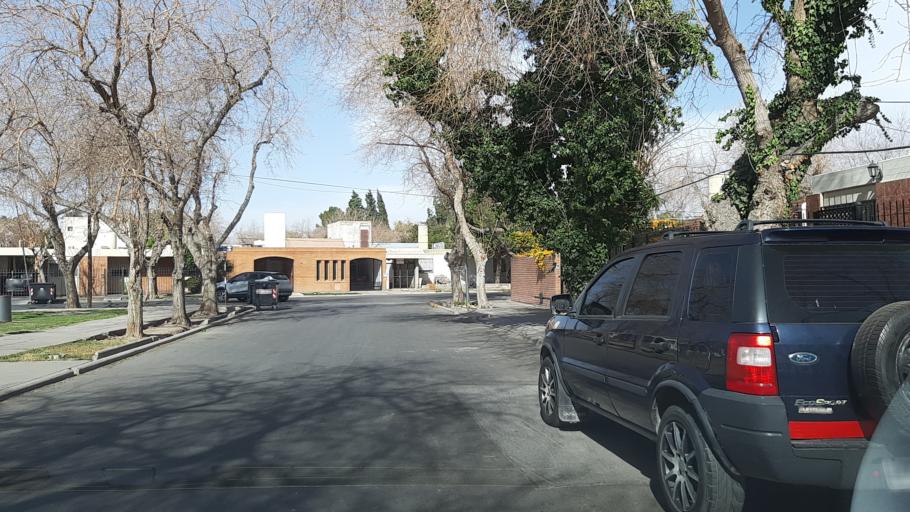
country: AR
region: San Juan
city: San Juan
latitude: -31.5266
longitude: -68.5458
